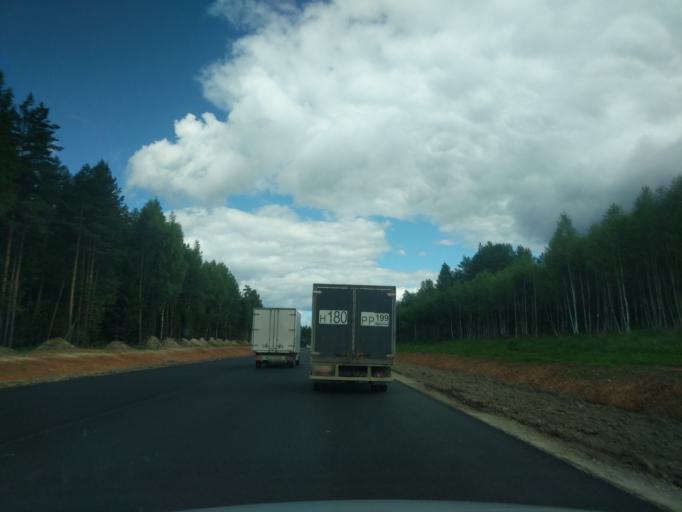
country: RU
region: Kostroma
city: Sudislavl'
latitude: 57.8226
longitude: 41.4939
